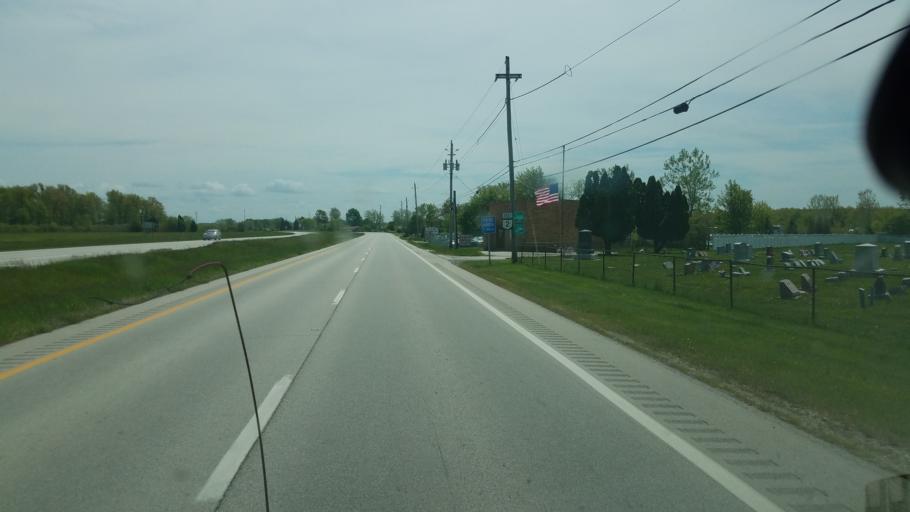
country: US
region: Ohio
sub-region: Ottawa County
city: Port Clinton
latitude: 41.5372
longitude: -83.0341
